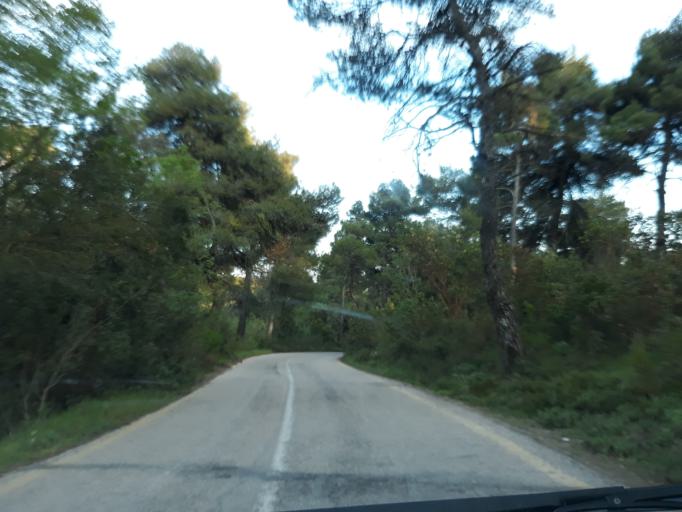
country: GR
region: Attica
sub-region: Nomarchia Anatolikis Attikis
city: Afidnes
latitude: 38.2124
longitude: 23.7891
